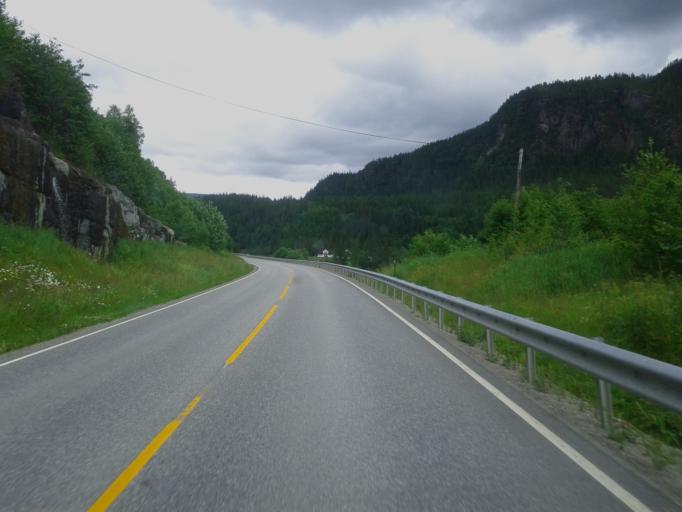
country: NO
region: Sor-Trondelag
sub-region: Midtre Gauldal
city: Storen
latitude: 62.9427
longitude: 10.6719
